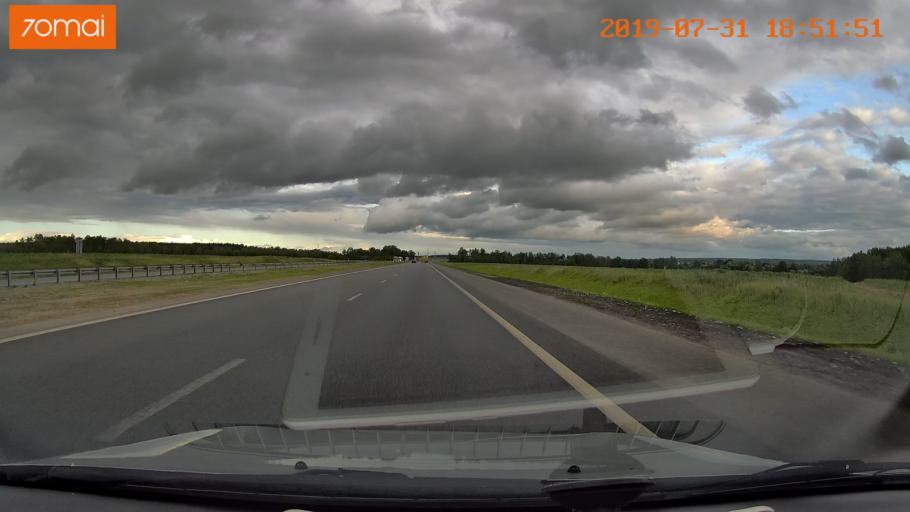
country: RU
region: Moskovskaya
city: Voskresensk
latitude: 55.2186
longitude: 38.6174
